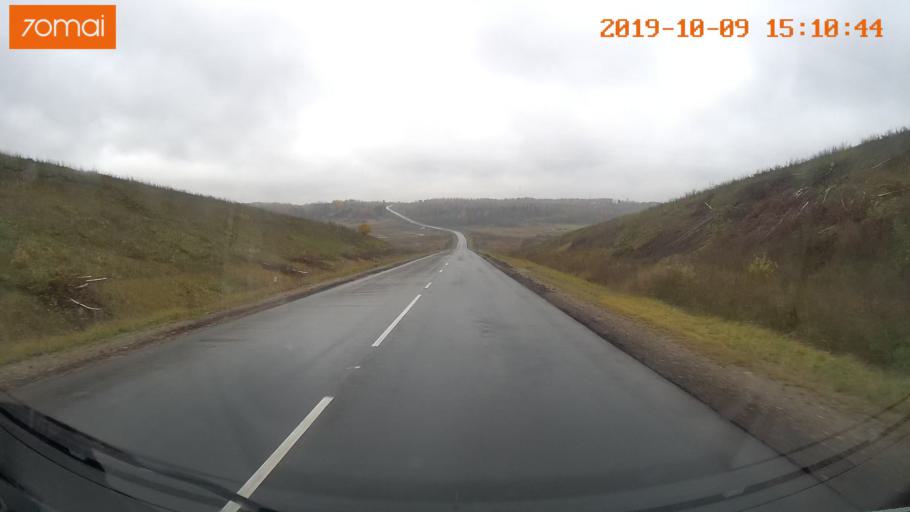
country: RU
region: Kostroma
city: Susanino
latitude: 58.1745
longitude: 41.6370
